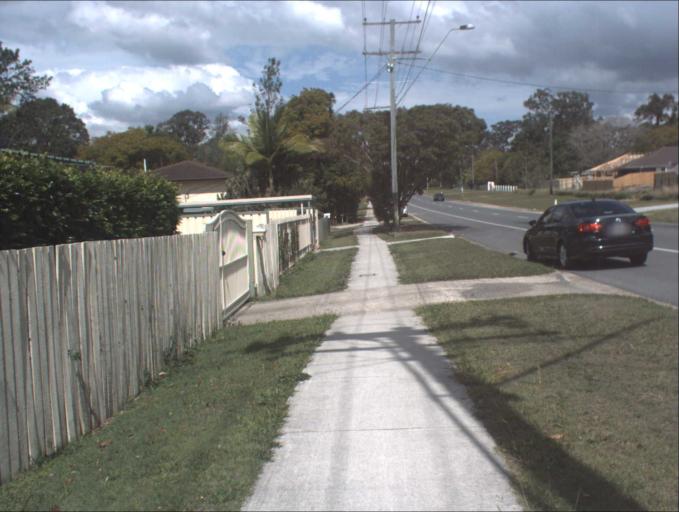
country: AU
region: Queensland
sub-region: Logan
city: Park Ridge South
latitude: -27.6919
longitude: 153.0103
